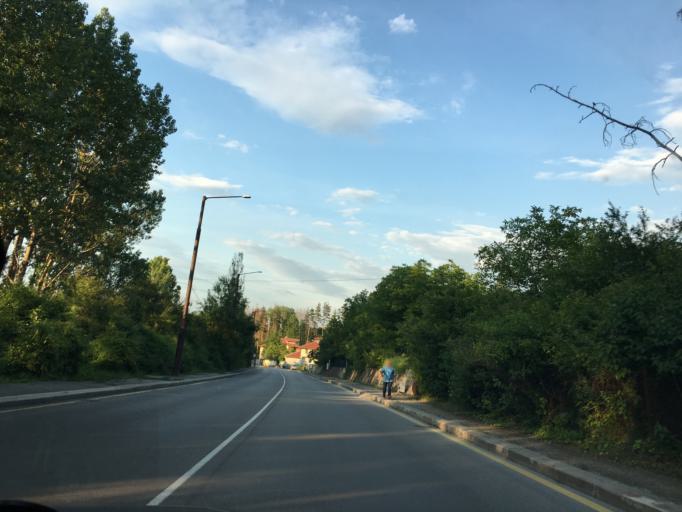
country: BG
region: Sofiya
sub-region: Obshtina Bozhurishte
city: Bozhurishte
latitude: 42.7092
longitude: 23.1593
